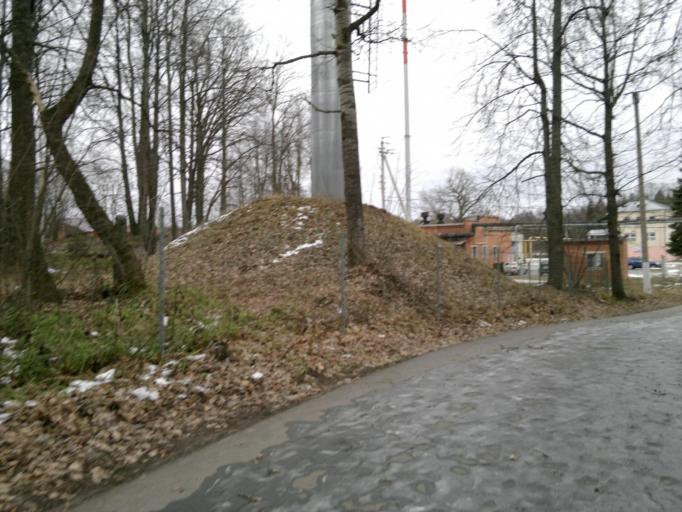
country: RU
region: Mariy-El
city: Yoshkar-Ola
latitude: 56.5991
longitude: 47.9700
